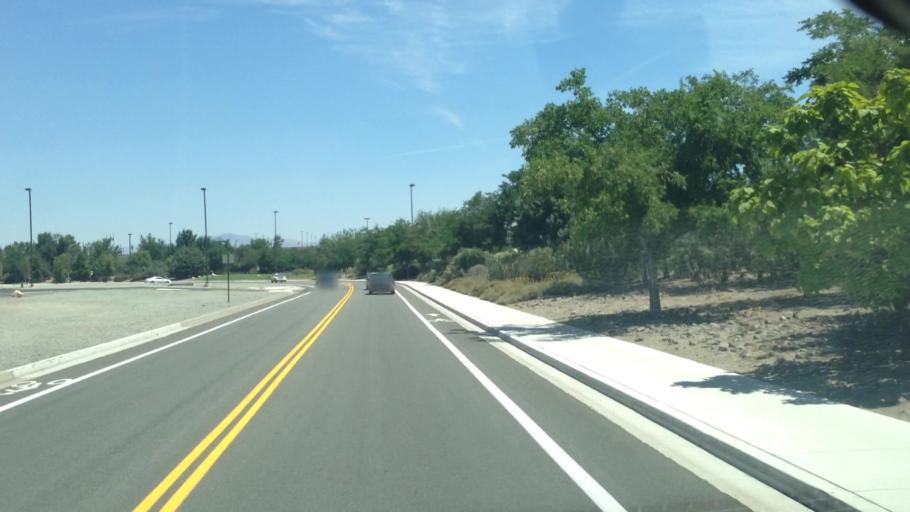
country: US
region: Nevada
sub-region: Washoe County
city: Sparks
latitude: 39.5029
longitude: -119.7802
